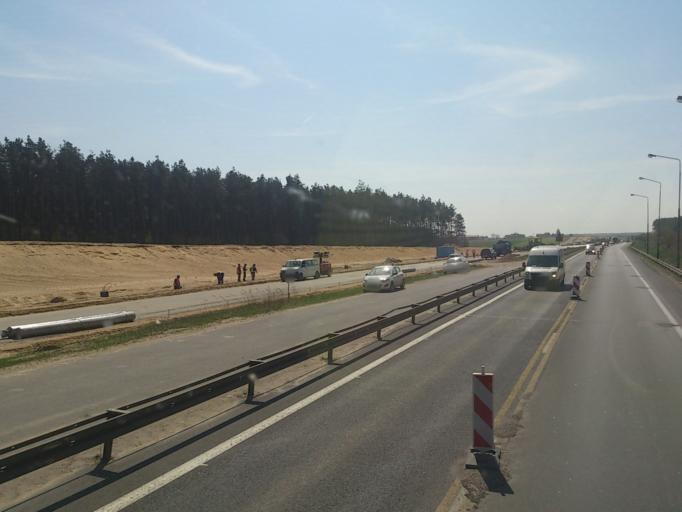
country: PL
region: Lodz Voivodeship
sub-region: Powiat piotrkowski
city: Czarnocin
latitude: 51.5440
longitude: 19.6028
